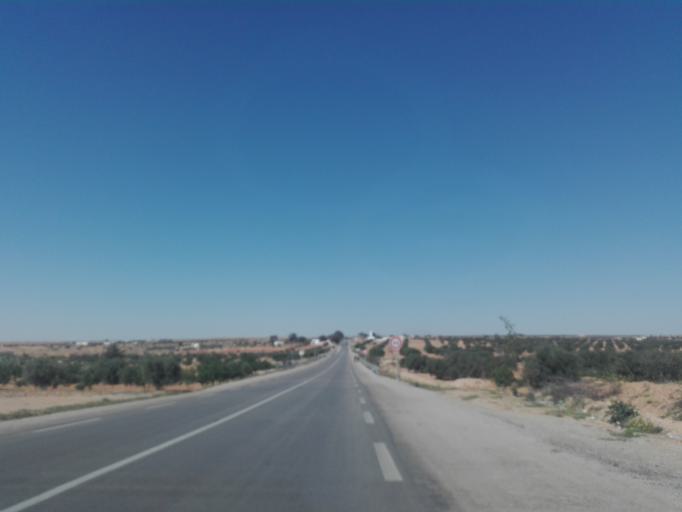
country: TN
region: Safaqis
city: Bi'r `Ali Bin Khalifah
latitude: 34.7411
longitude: 10.3805
